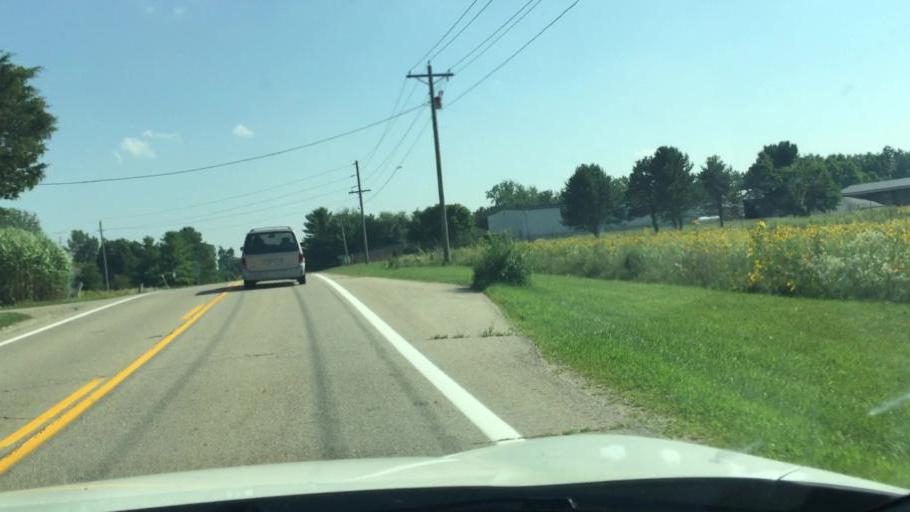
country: US
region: Ohio
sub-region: Champaign County
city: Mechanicsburg
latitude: 40.1239
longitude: -83.5324
